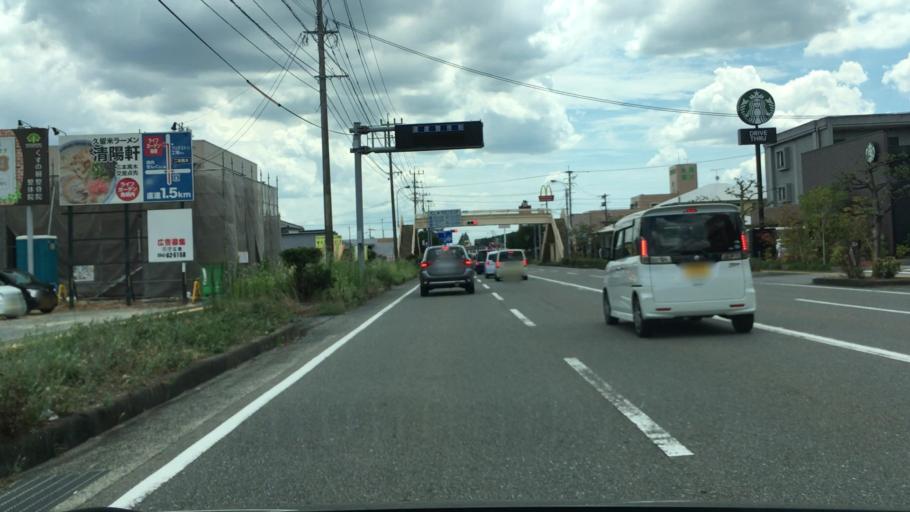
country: JP
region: Saga Prefecture
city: Tosu
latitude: 33.3763
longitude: 130.4988
